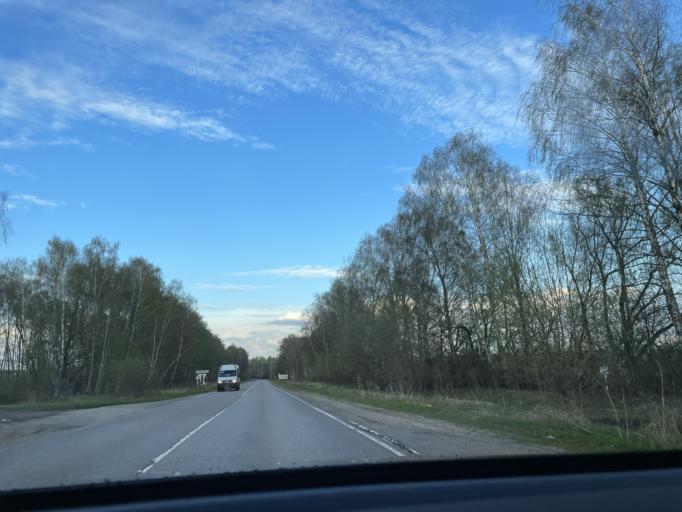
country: RU
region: Tula
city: Novogurovskiy
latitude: 54.5193
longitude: 37.2360
